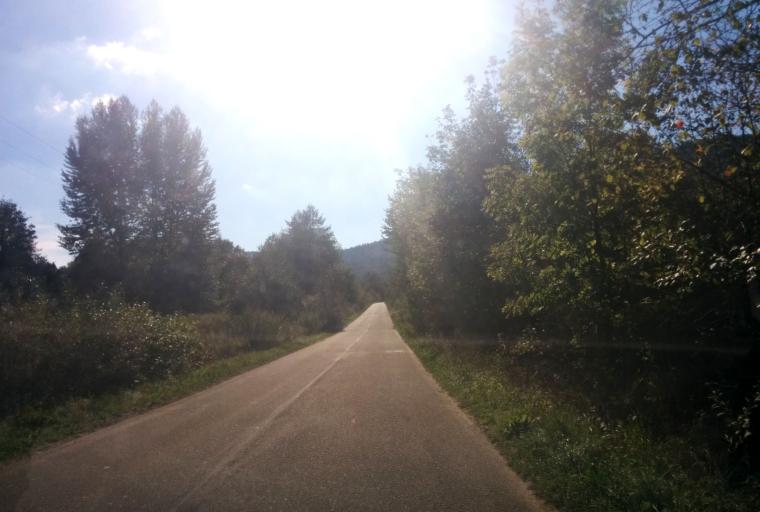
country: PL
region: Subcarpathian Voivodeship
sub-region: Powiat leski
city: Polanczyk
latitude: 49.2900
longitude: 22.4191
